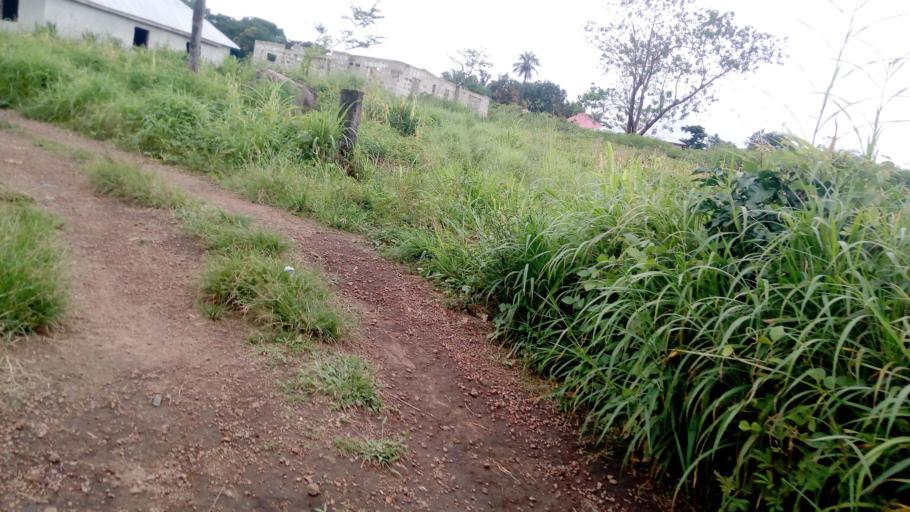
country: SL
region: Northern Province
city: Makeni
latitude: 8.8911
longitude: -12.0277
